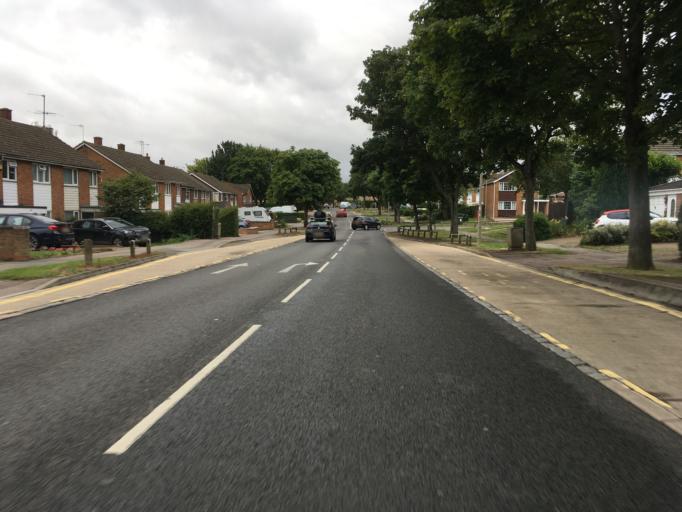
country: GB
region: England
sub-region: Buckinghamshire
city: Bletchley
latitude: 52.0095
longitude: -0.7488
